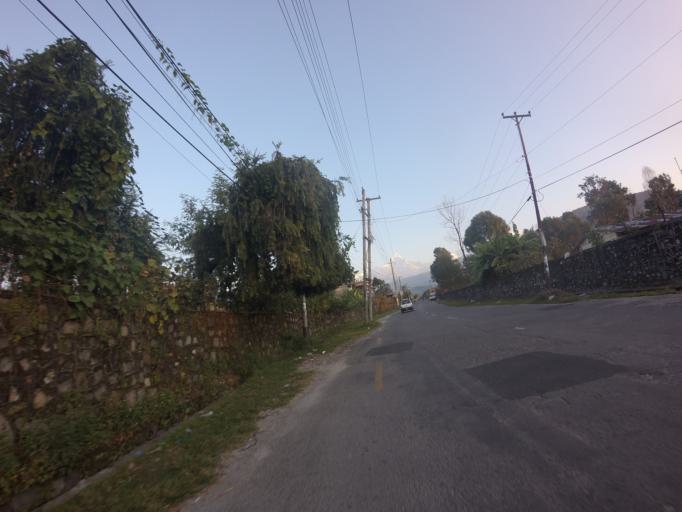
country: NP
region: Western Region
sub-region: Gandaki Zone
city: Pokhara
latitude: 28.2142
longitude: 83.9981
